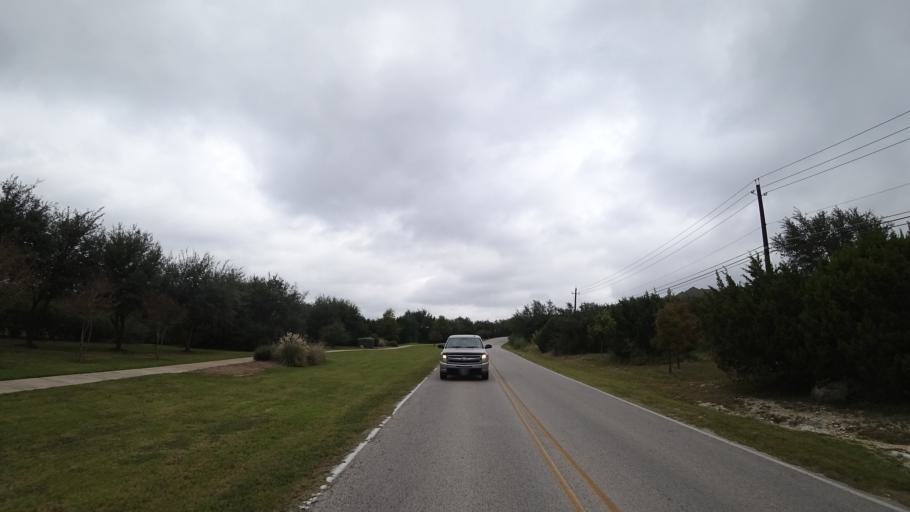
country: US
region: Texas
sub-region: Travis County
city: Bee Cave
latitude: 30.3418
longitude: -97.9210
